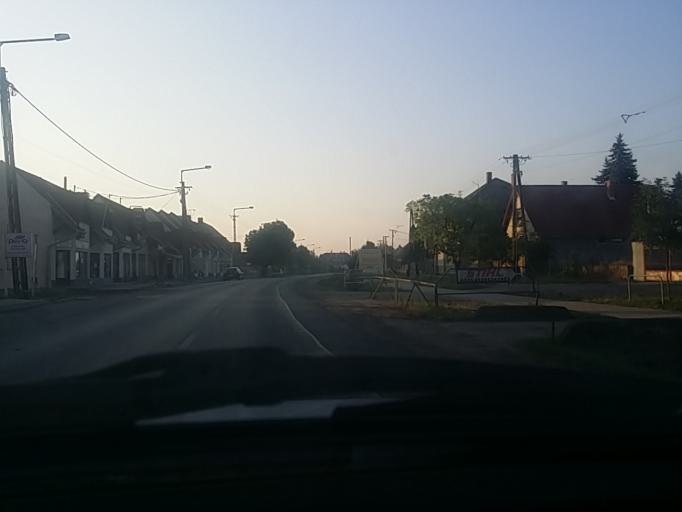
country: HU
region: Pest
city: Nagykata
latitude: 47.4174
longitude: 19.7467
